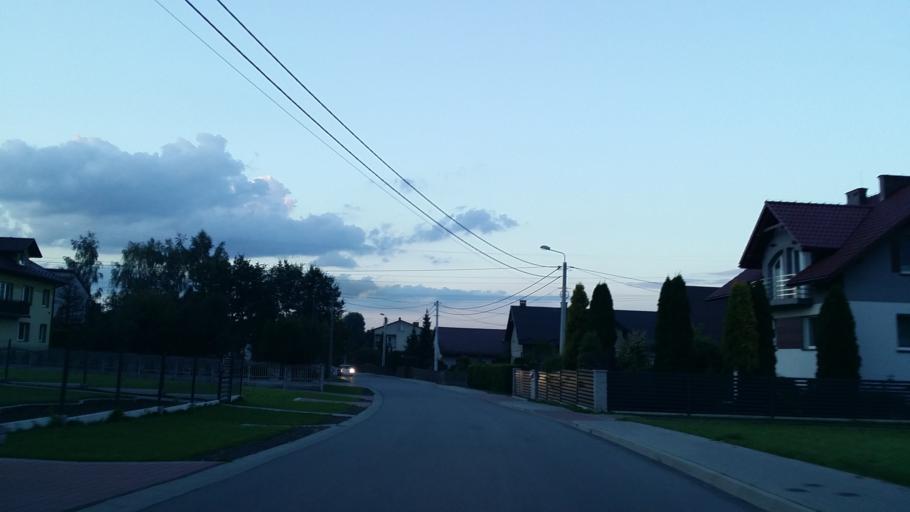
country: PL
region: Lesser Poland Voivodeship
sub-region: Powiat oswiecimski
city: Przeciszow
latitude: 50.0027
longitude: 19.3647
